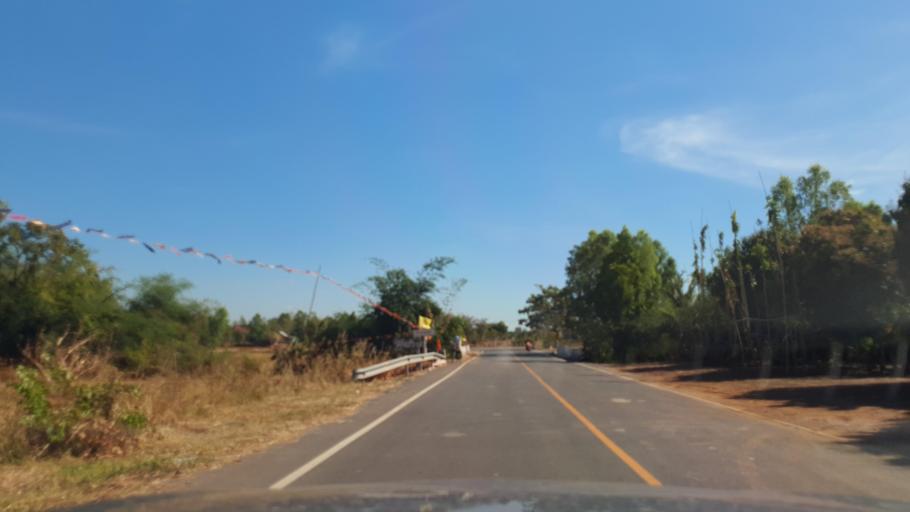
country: TH
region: Kalasin
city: Khao Wong
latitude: 16.7281
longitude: 104.0990
